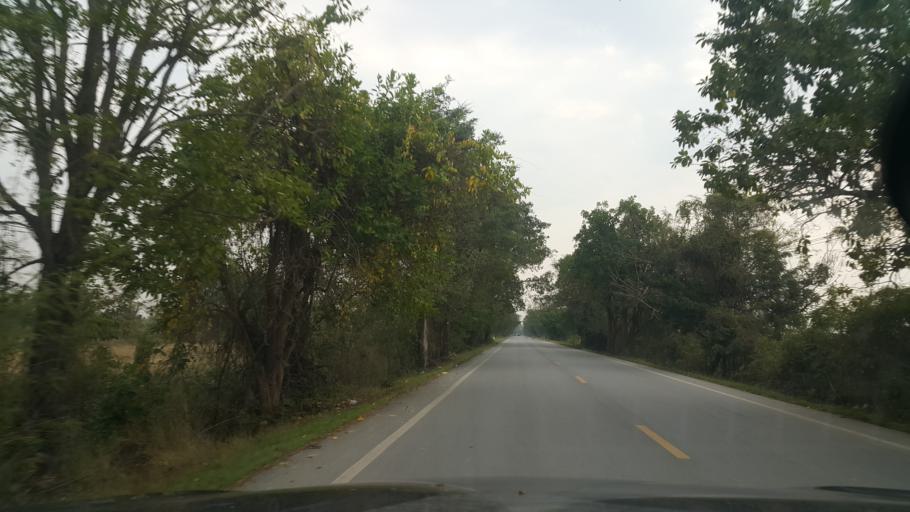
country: TH
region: Sukhothai
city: Si Samrong
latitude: 17.1701
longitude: 99.7181
